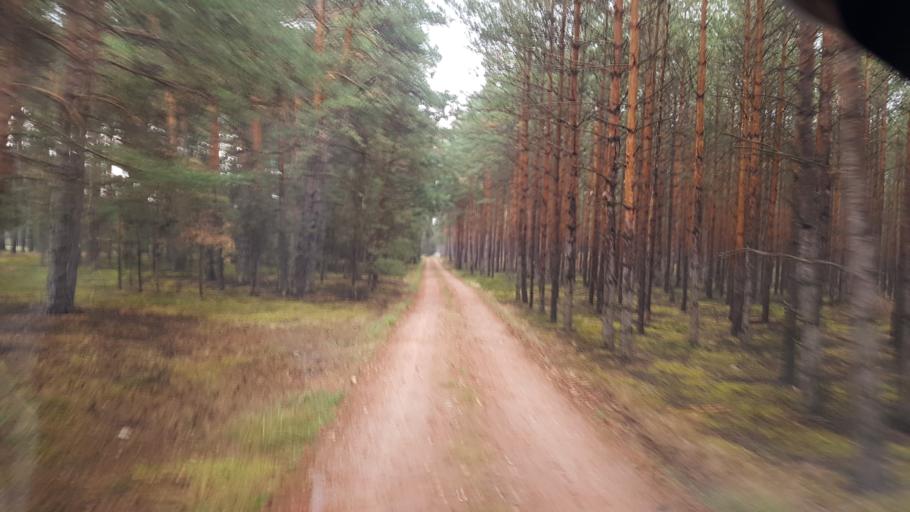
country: DE
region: Brandenburg
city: Sallgast
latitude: 51.6381
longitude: 13.7904
